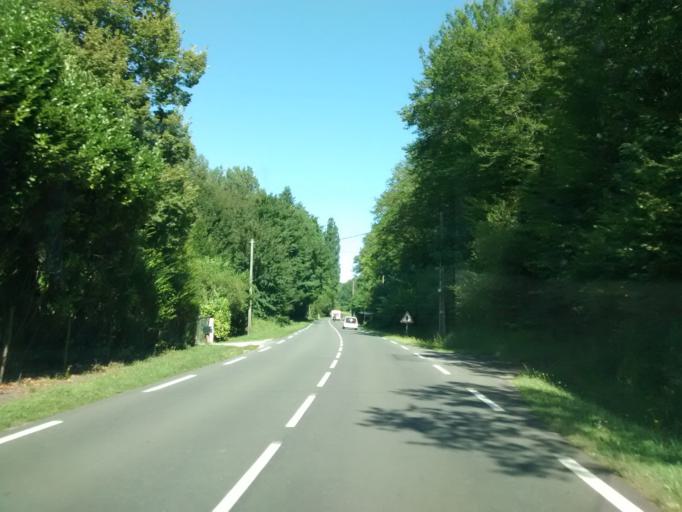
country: FR
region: Aquitaine
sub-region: Departement de la Dordogne
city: Saint-Cyprien
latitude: 44.9433
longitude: 1.0372
